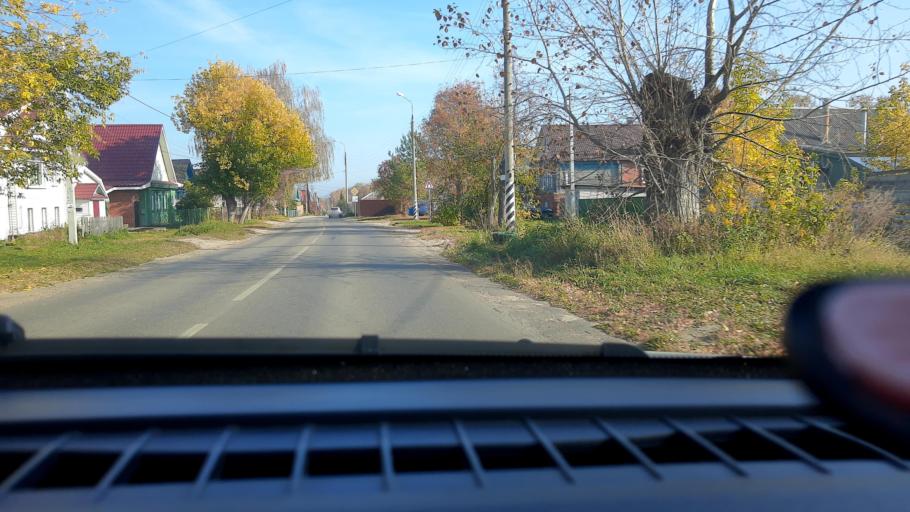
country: RU
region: Nizjnij Novgorod
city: Kstovo
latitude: 56.1545
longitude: 44.2375
